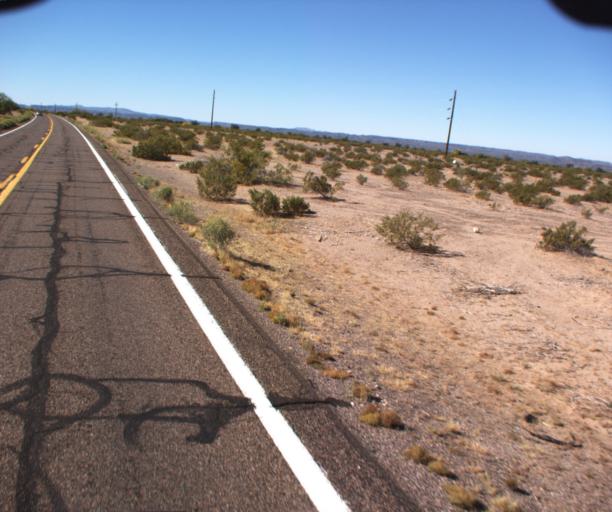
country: US
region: Arizona
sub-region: Maricopa County
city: Gila Bend
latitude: 32.6875
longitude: -112.8544
